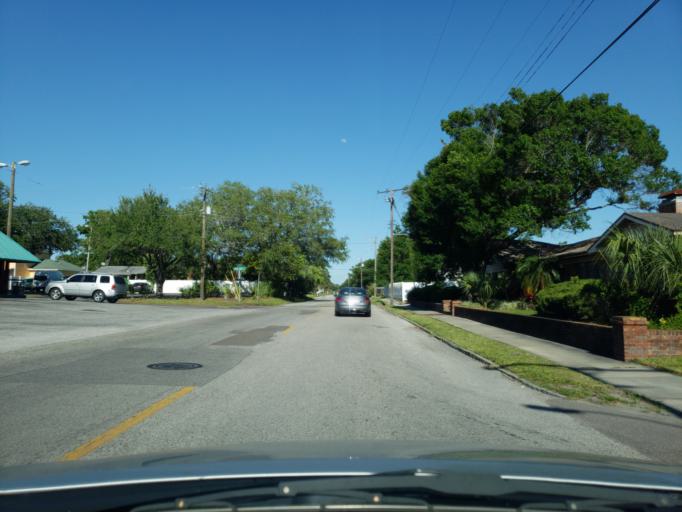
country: US
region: Florida
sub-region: Hillsborough County
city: Tampa
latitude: 27.9520
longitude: -82.4902
